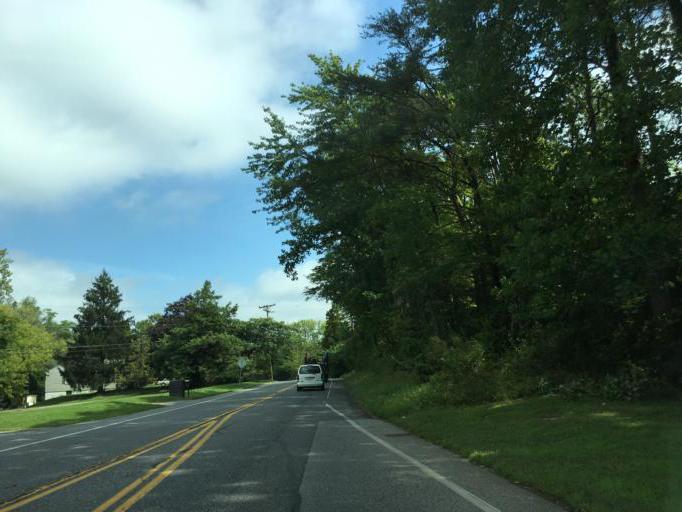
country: US
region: Maryland
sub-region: Anne Arundel County
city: Crownsville
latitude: 39.0151
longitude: -76.5965
